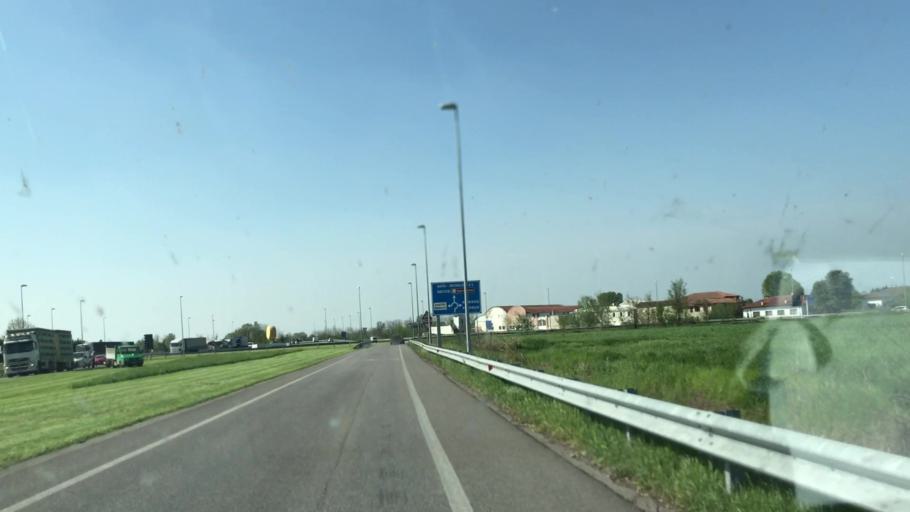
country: IT
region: Lombardy
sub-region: Provincia di Mantova
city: Marmirolo
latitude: 45.2189
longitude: 10.7453
